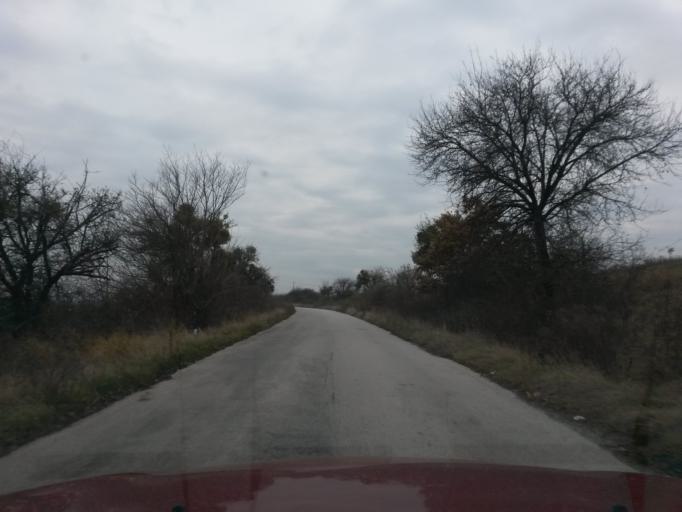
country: SK
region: Kosicky
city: Kosice
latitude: 48.7303
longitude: 21.4475
